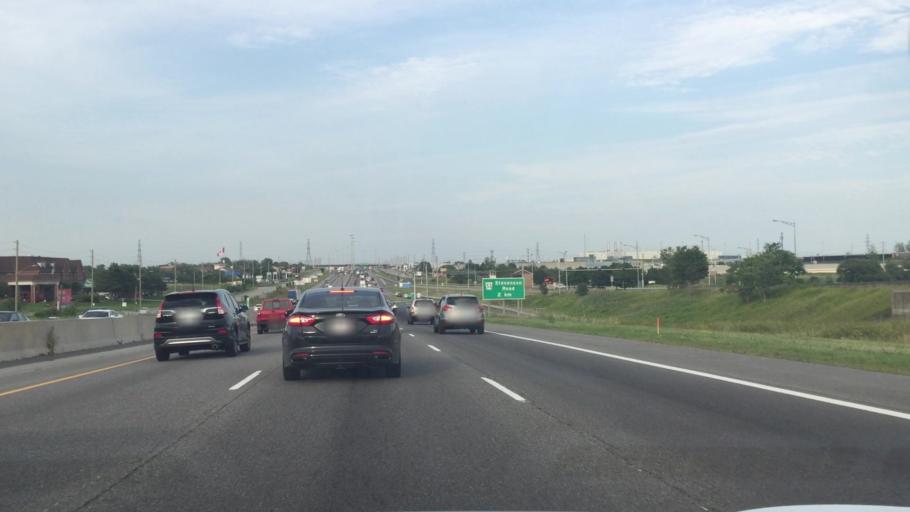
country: CA
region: Ontario
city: Oshawa
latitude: 43.8699
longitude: -78.8996
